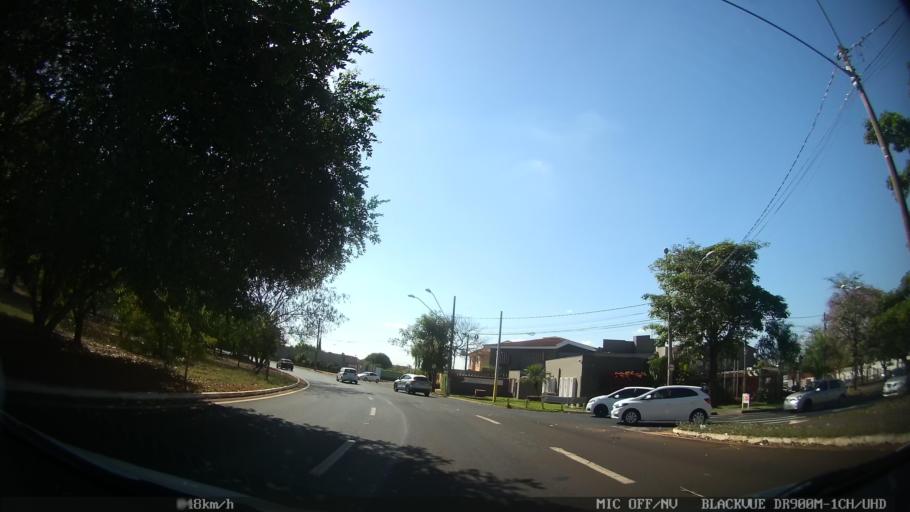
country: BR
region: Sao Paulo
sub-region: Ribeirao Preto
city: Ribeirao Preto
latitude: -21.1935
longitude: -47.7602
